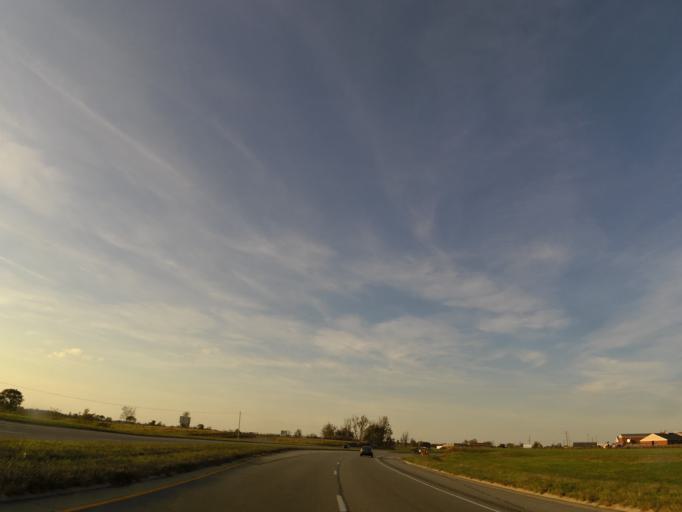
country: US
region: Kentucky
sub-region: Garrard County
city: Lancaster
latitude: 37.6924
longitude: -84.6645
